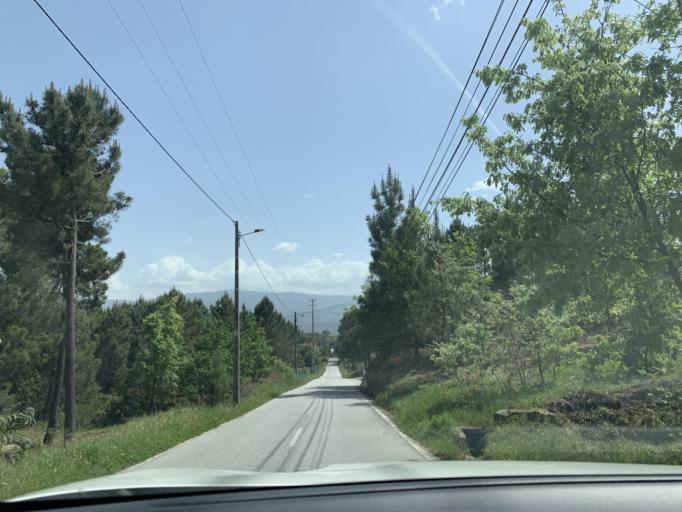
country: PT
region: Guarda
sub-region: Fornos de Algodres
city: Fornos de Algodres
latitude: 40.5945
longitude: -7.6302
